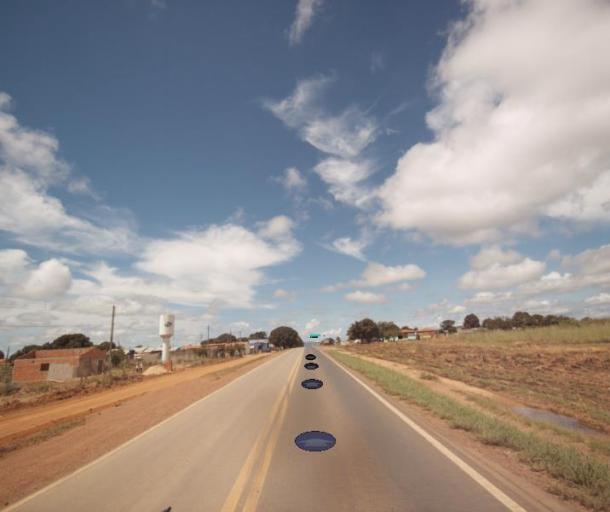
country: BR
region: Goias
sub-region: Padre Bernardo
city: Padre Bernardo
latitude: -15.2504
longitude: -48.2685
